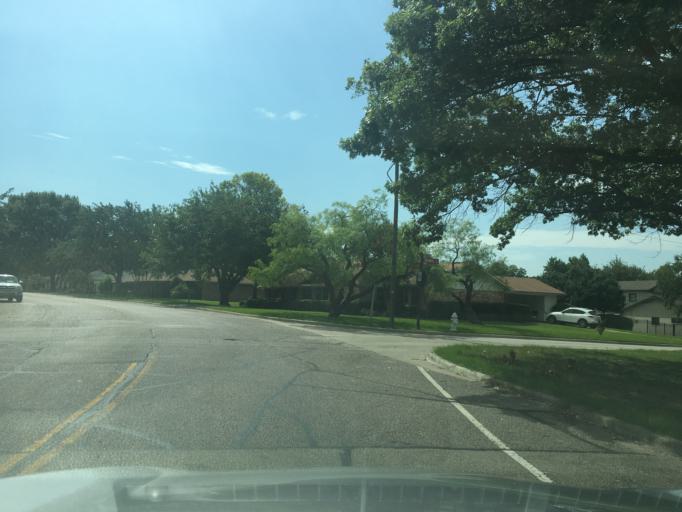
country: US
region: Texas
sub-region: Dallas County
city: Carrollton
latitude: 32.9422
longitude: -96.8609
